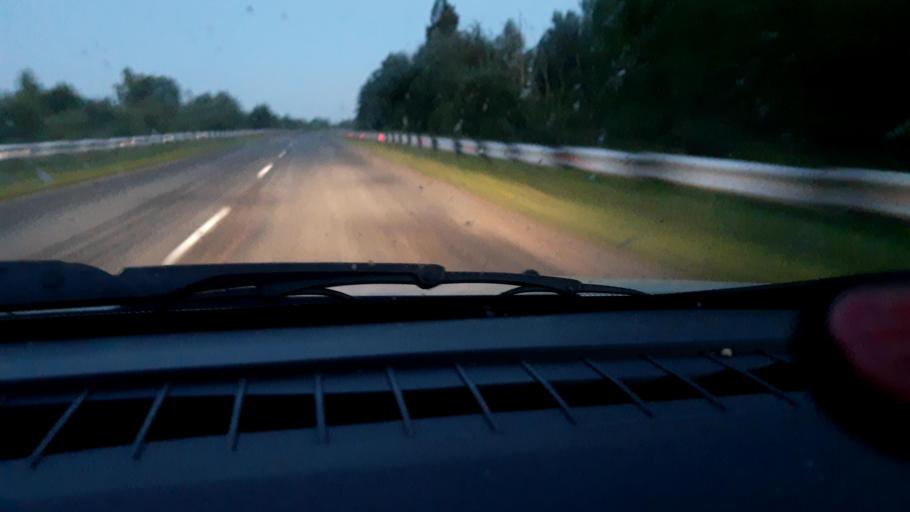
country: RU
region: Nizjnij Novgorod
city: Tonkino
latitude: 57.3662
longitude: 46.4231
